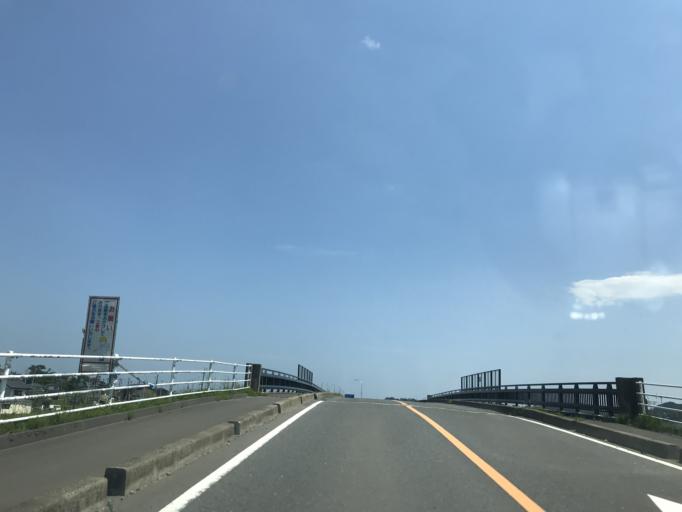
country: JP
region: Miyagi
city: Matsushima
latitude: 38.3707
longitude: 141.1429
